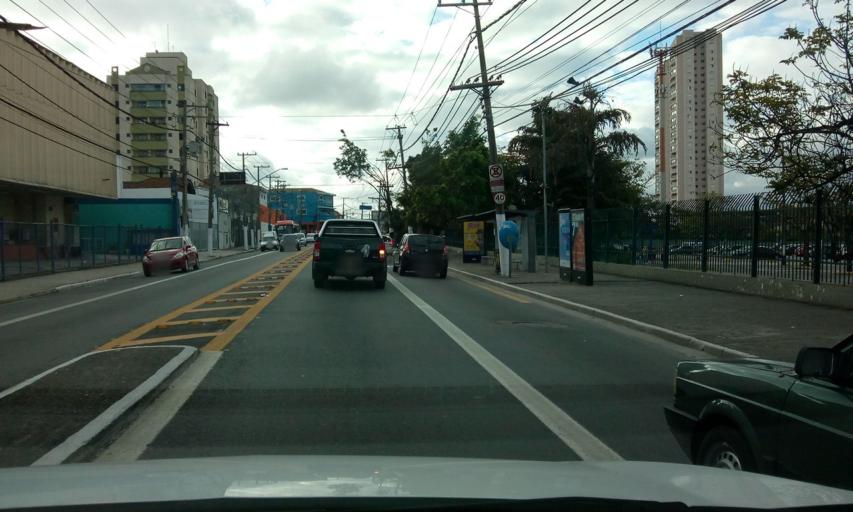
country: BR
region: Sao Paulo
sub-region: Sao Caetano Do Sul
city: Sao Caetano do Sul
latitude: -23.5619
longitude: -46.5173
